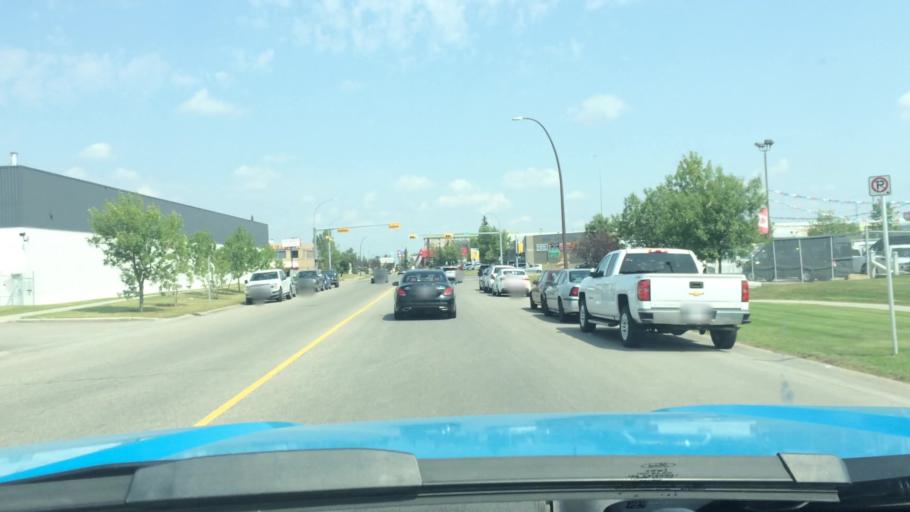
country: CA
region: Alberta
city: Calgary
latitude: 51.0724
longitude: -114.0041
